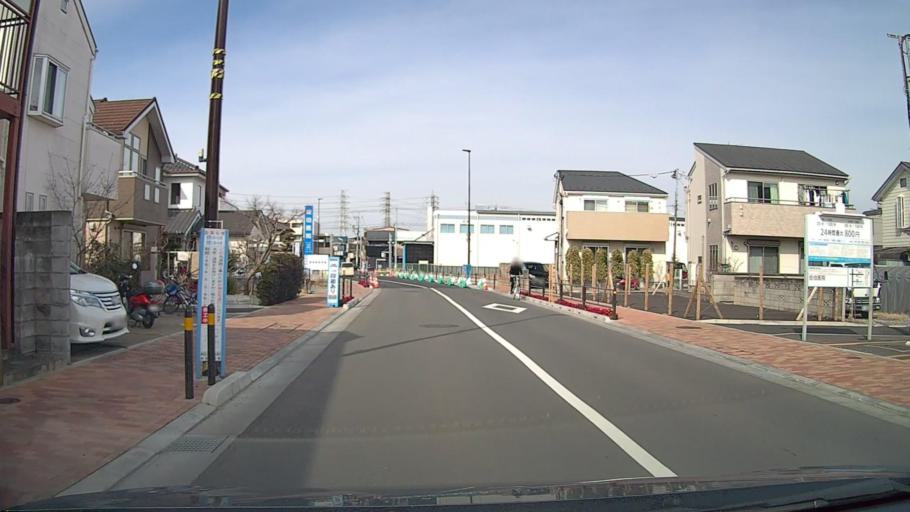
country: JP
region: Tokyo
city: Tanashicho
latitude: 35.7598
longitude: 139.5664
